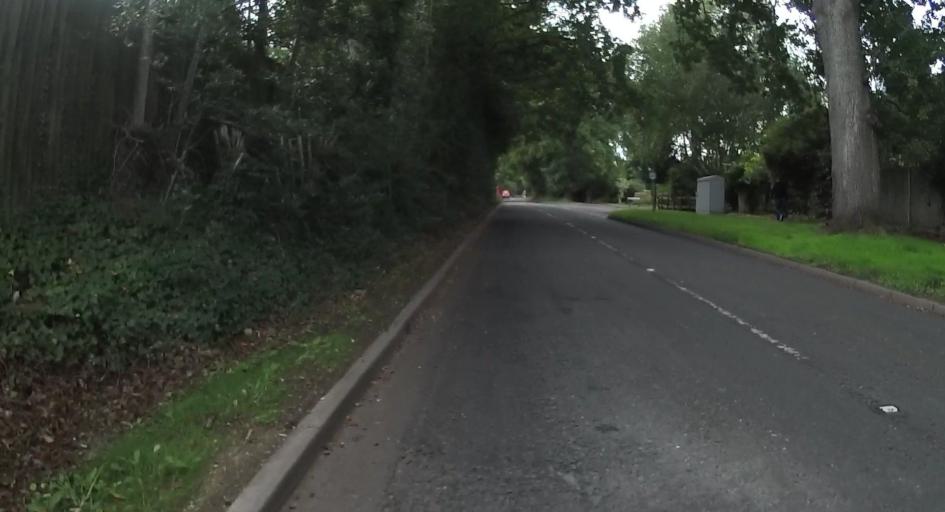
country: GB
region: England
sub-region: Surrey
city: Windlesham
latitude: 51.3468
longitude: -0.6667
